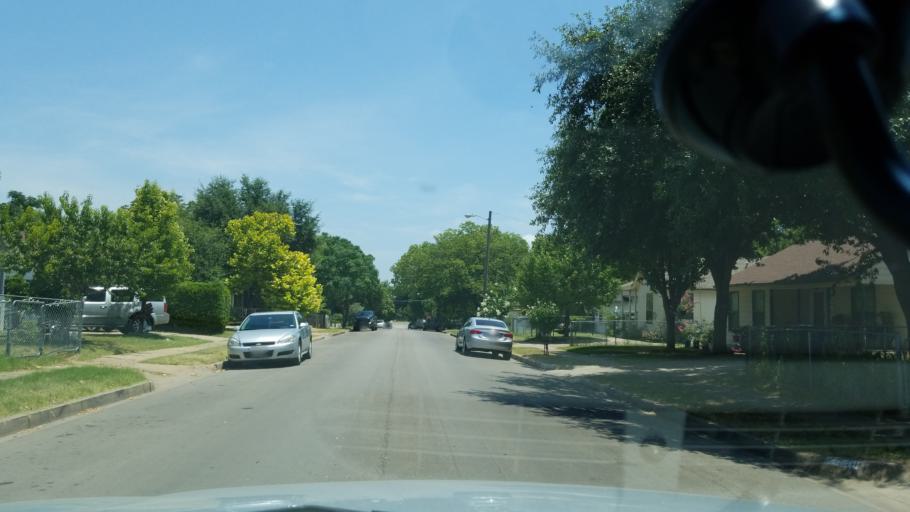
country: US
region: Texas
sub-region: Dallas County
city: Cockrell Hill
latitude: 32.7302
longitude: -96.8608
